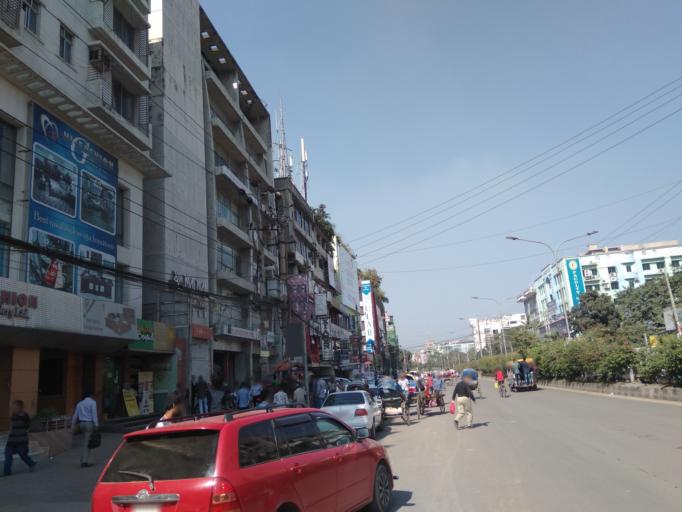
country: BD
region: Dhaka
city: Azimpur
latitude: 23.7399
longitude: 90.3751
